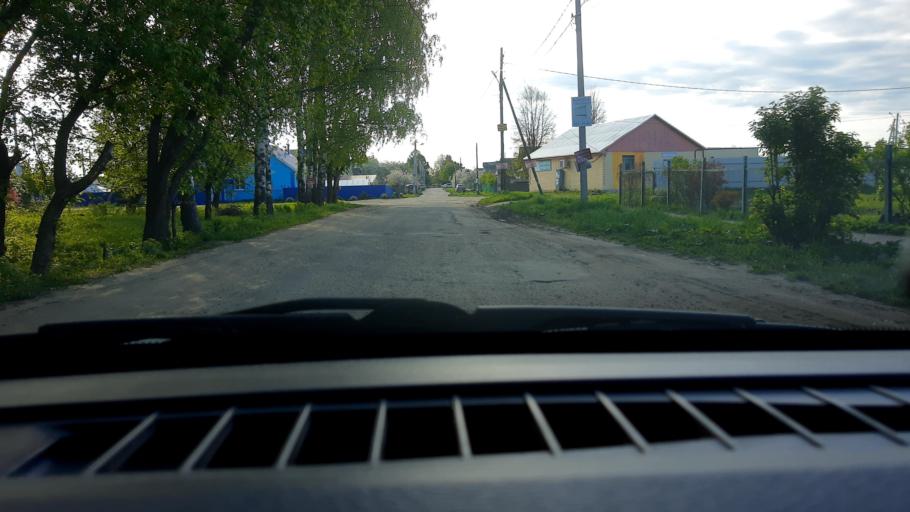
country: RU
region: Nizjnij Novgorod
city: Neklyudovo
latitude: 56.4082
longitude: 44.0325
